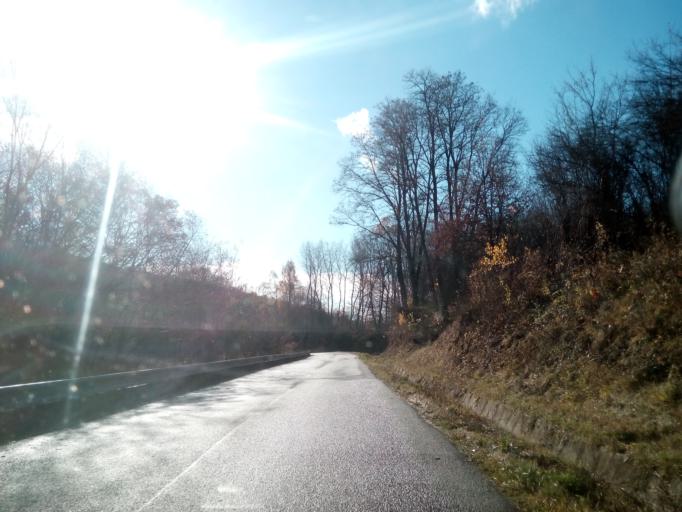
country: SK
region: Presovsky
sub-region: Okres Bardejov
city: Bardejov
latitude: 49.3510
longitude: 21.3410
